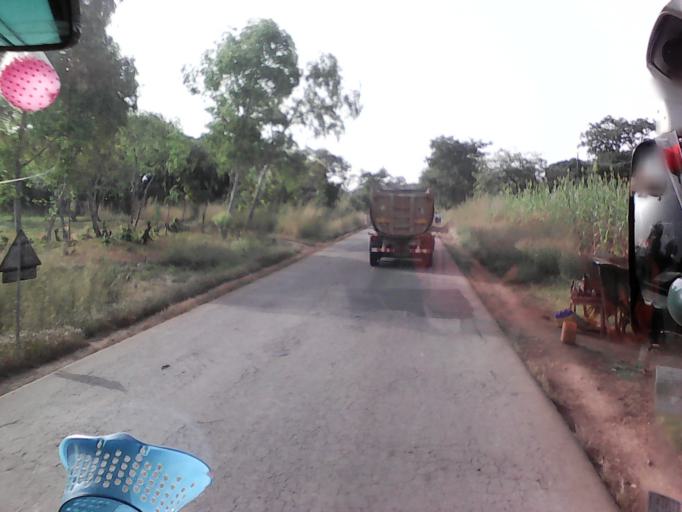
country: TG
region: Kara
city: Kara
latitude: 9.4775
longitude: 1.2110
